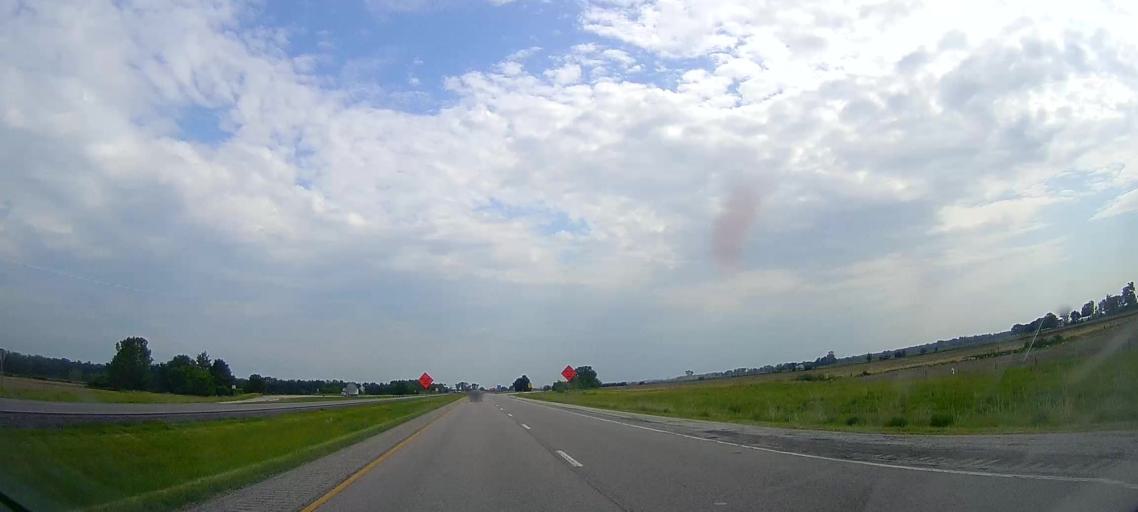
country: US
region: Nebraska
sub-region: Burt County
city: Tekamah
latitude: 41.7464
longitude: -96.0471
